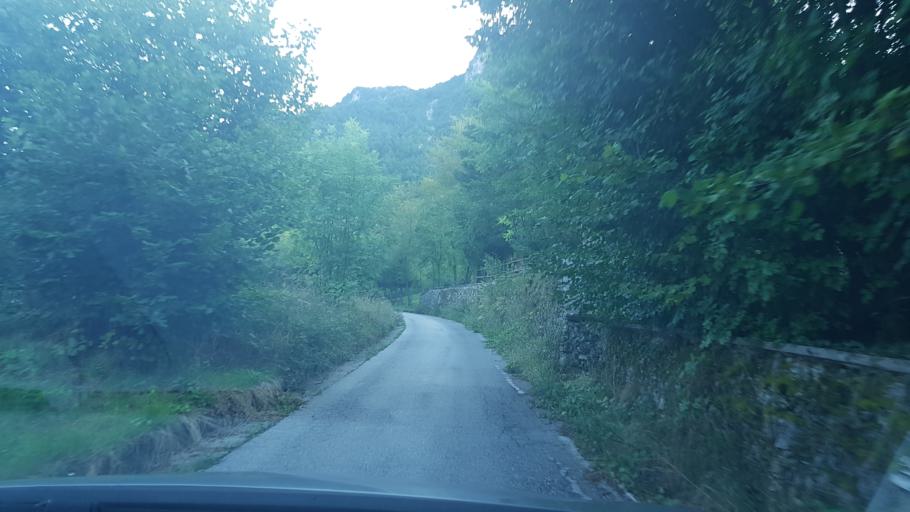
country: IT
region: Friuli Venezia Giulia
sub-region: Provincia di Udine
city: Moggio Udinese
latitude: 46.4293
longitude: 13.2055
